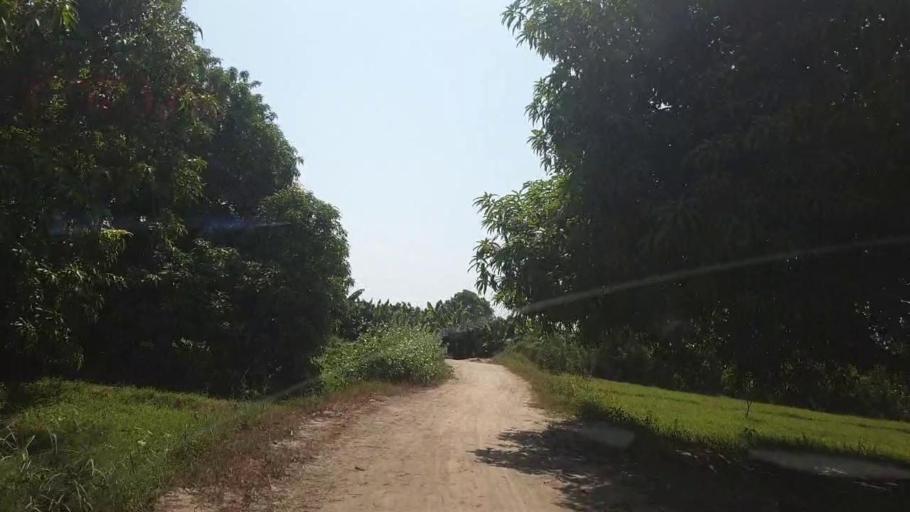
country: PK
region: Sindh
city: Tando Allahyar
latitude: 25.3936
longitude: 68.6696
